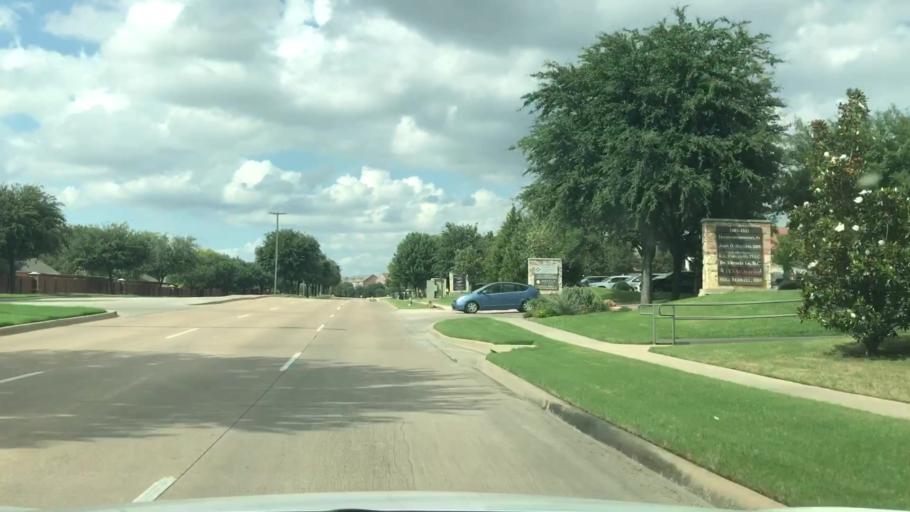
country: US
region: Texas
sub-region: Dallas County
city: Coppell
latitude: 32.9091
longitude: -96.9633
